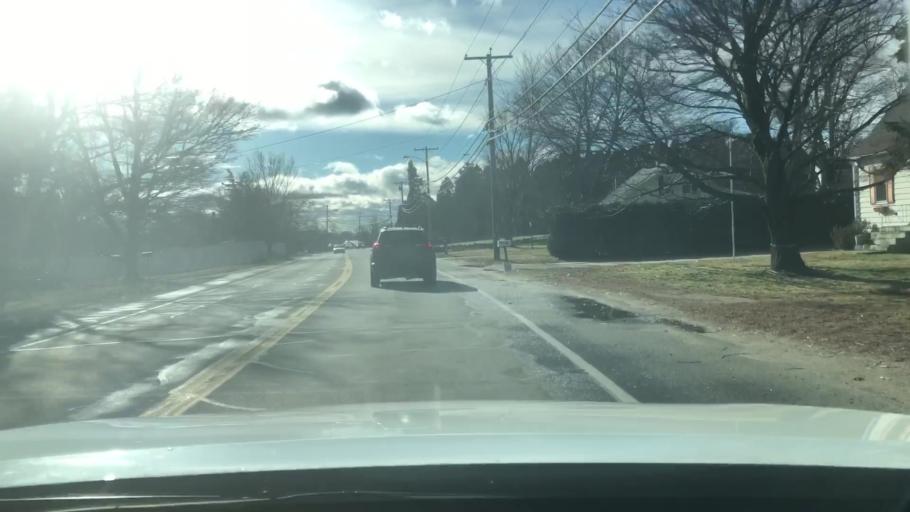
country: US
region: Massachusetts
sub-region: Norfolk County
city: Bellingham
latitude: 42.0463
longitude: -71.4873
